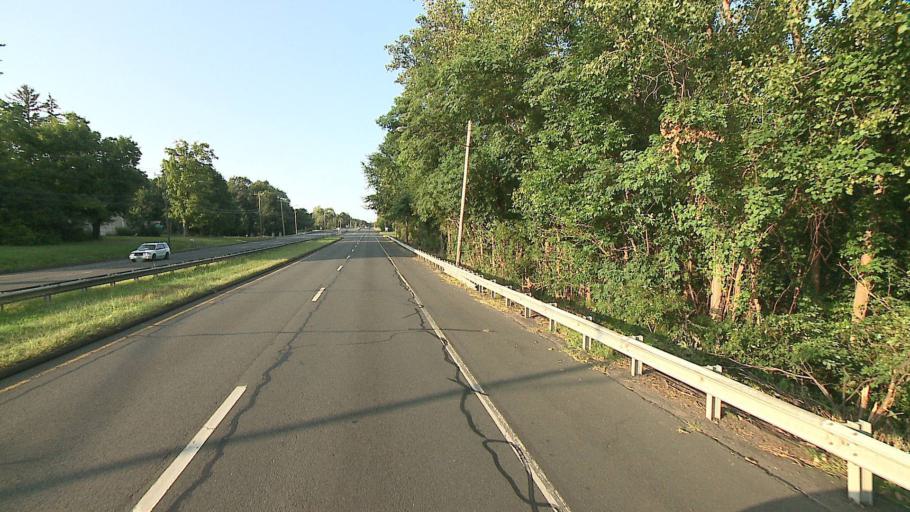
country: US
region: Connecticut
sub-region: Hartford County
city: Kensington
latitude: 41.5937
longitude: -72.7573
